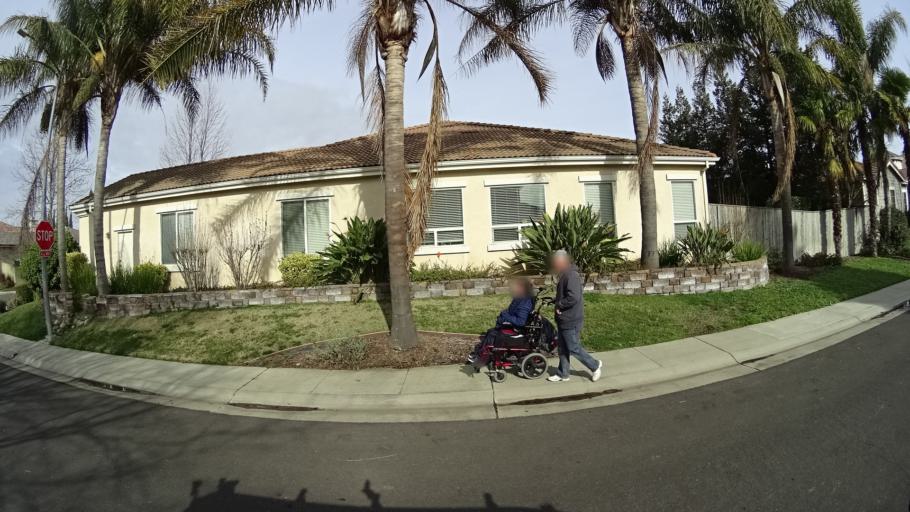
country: US
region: California
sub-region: Yolo County
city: Davis
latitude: 38.5504
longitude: -121.6770
